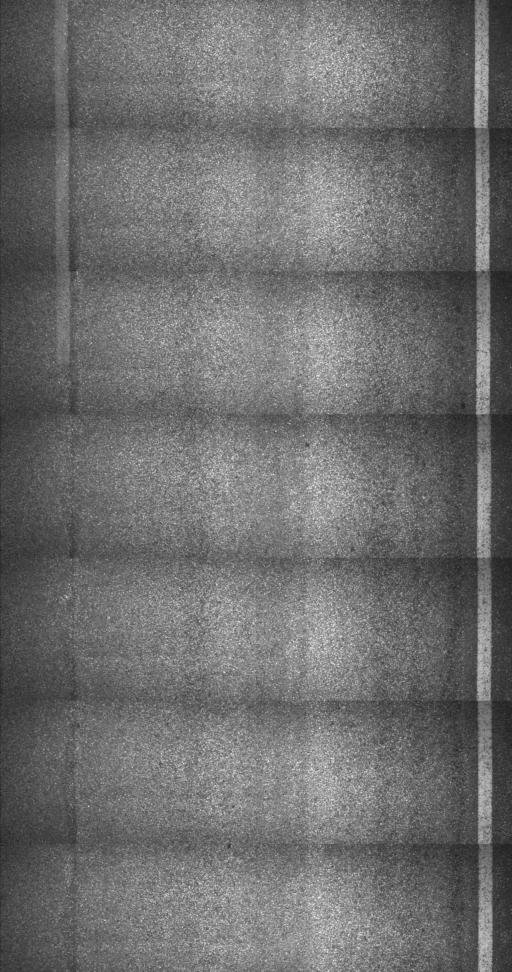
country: US
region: Vermont
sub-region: Grand Isle County
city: North Hero
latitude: 44.7462
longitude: -73.2885
